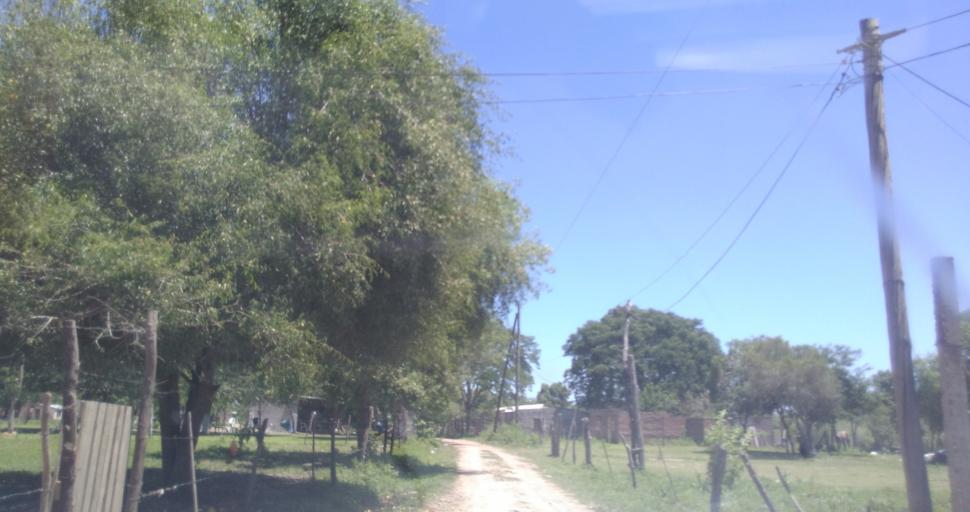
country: AR
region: Chaco
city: Fontana
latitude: -27.4146
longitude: -59.0092
